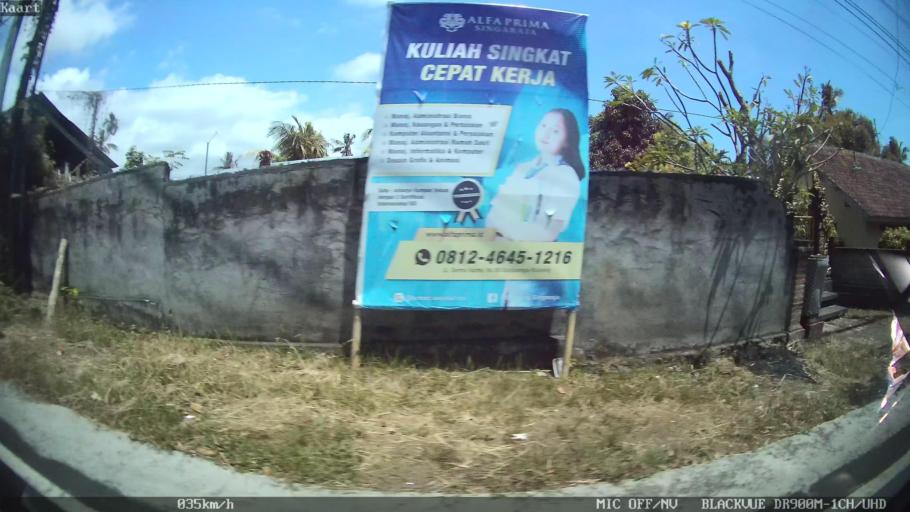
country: ID
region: Bali
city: Banjar Sambangan
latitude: -8.1522
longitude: 115.1075
